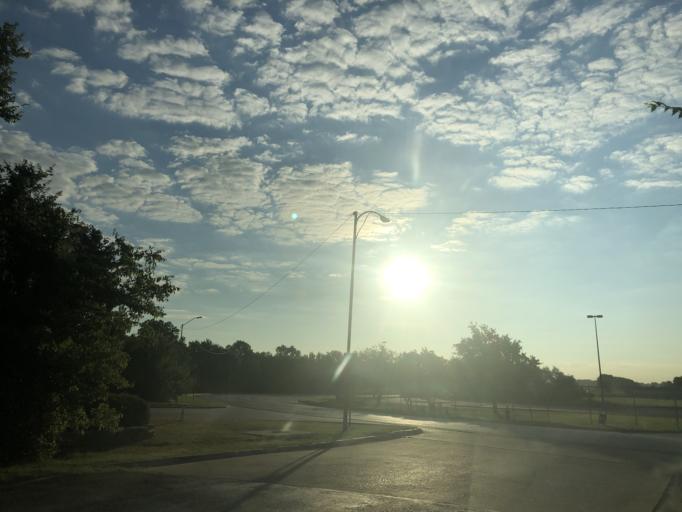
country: US
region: Texas
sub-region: Dallas County
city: Grand Prairie
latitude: 32.7619
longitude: -97.0061
